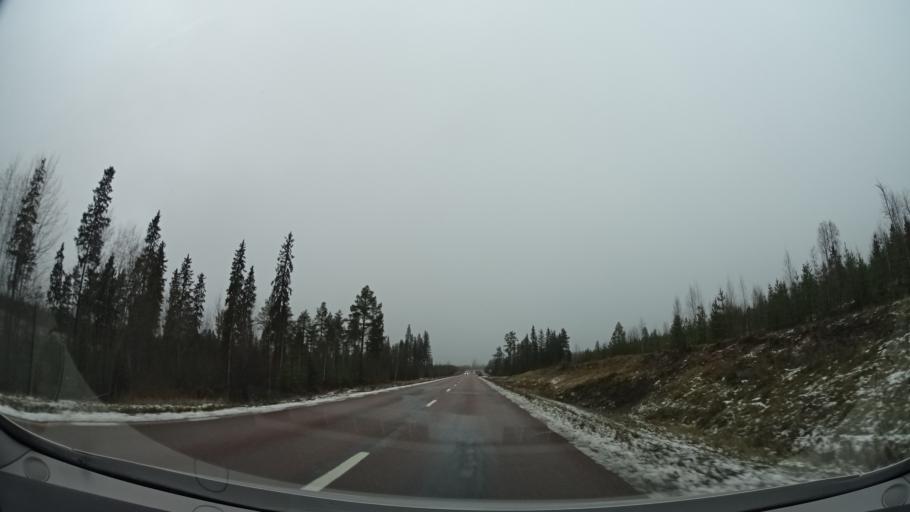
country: SE
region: Vaesterbotten
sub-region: Dorotea Kommun
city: Dorotea
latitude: 64.1356
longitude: 16.2239
